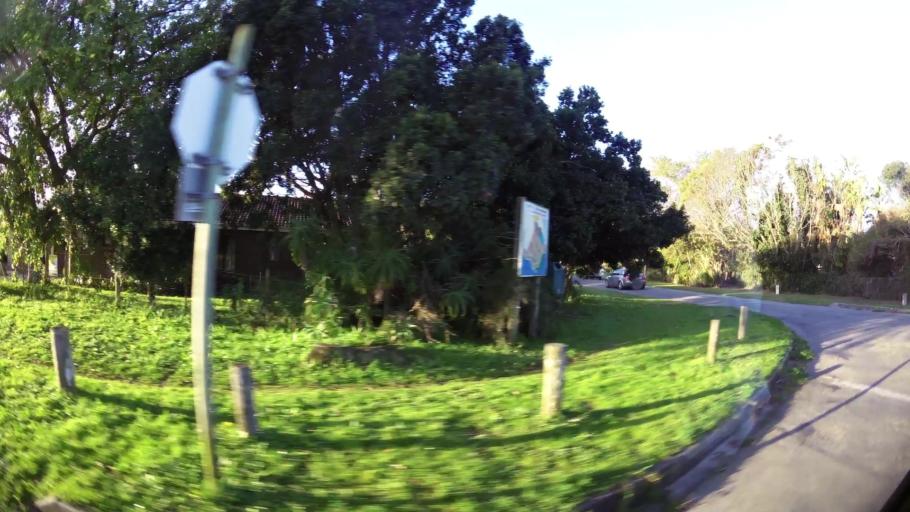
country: ZA
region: Western Cape
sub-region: Eden District Municipality
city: Knysna
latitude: -34.0164
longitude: 22.7855
